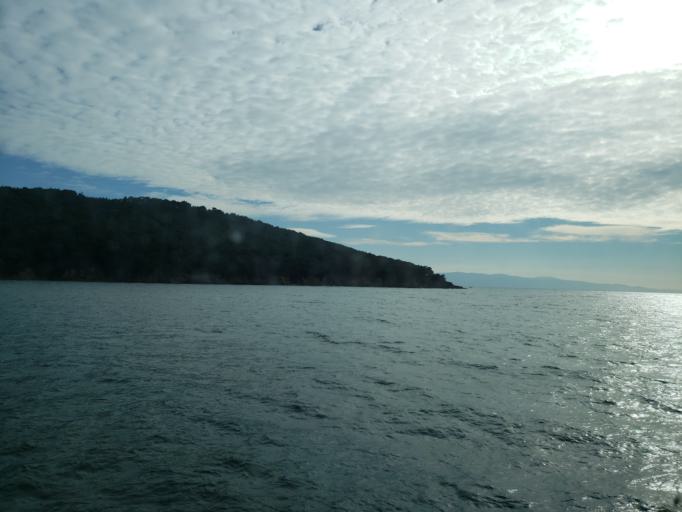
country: TR
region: Istanbul
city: Adalan
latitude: 40.8793
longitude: 29.0767
